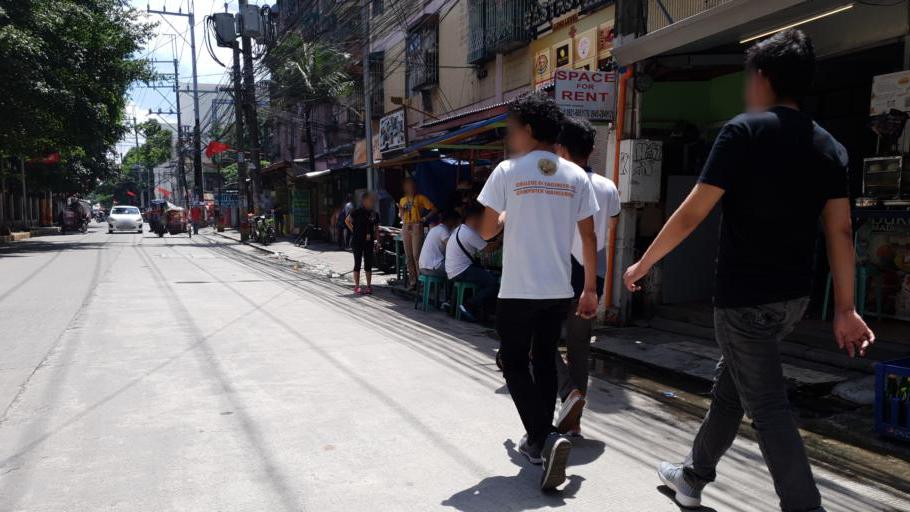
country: PH
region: Metro Manila
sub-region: City of Manila
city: Quiapo
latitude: 14.5987
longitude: 121.0053
